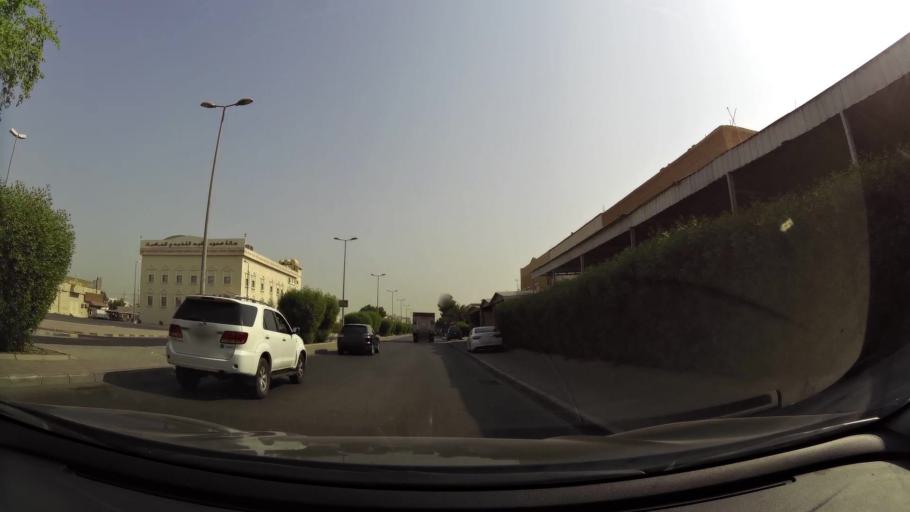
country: KW
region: Al Asimah
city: Ar Rabiyah
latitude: 29.2893
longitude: 47.8726
